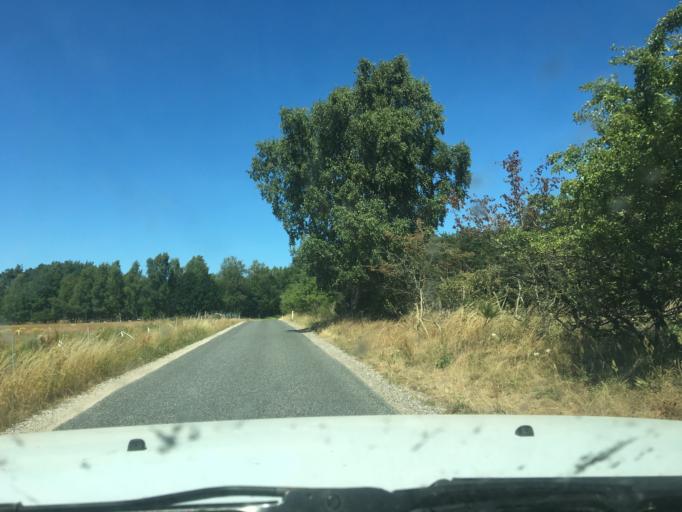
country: DK
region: Central Jutland
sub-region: Syddjurs Kommune
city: Ryomgard
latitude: 56.4827
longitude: 10.5939
